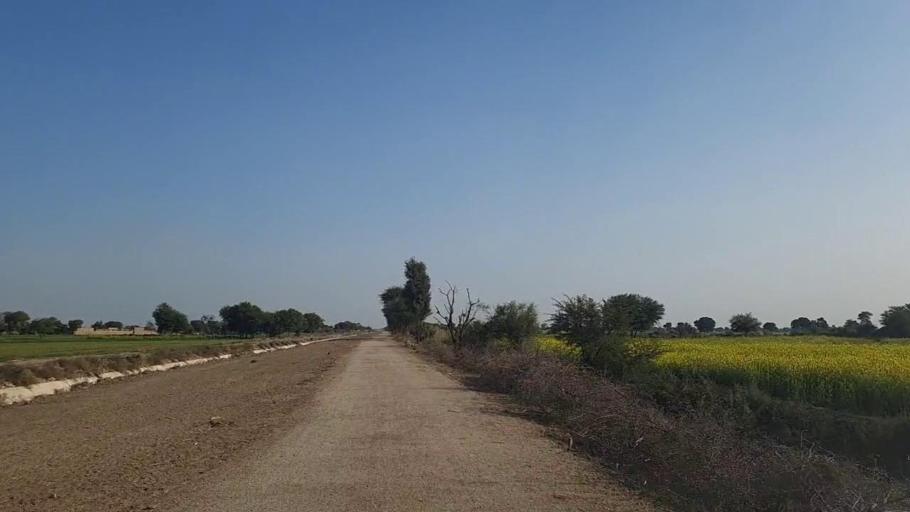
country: PK
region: Sindh
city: Shahpur Chakar
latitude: 26.2016
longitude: 68.6478
